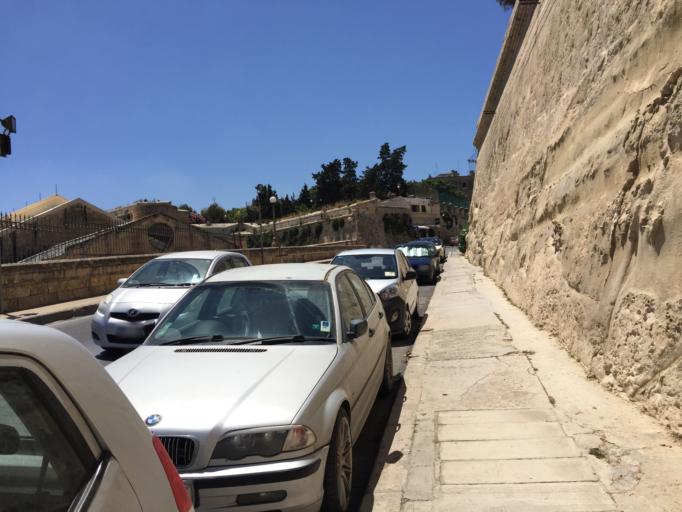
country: MT
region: Il-Furjana
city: Floriana
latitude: 35.8927
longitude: 14.5097
